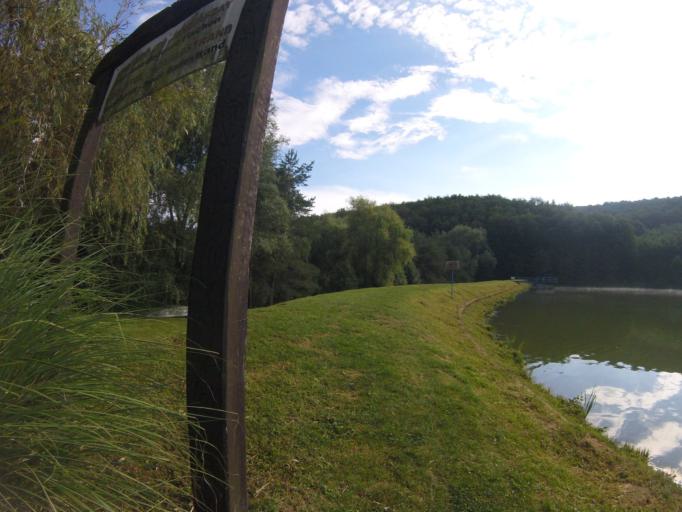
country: HU
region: Zala
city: Becsehely
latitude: 46.4923
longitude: 16.7433
